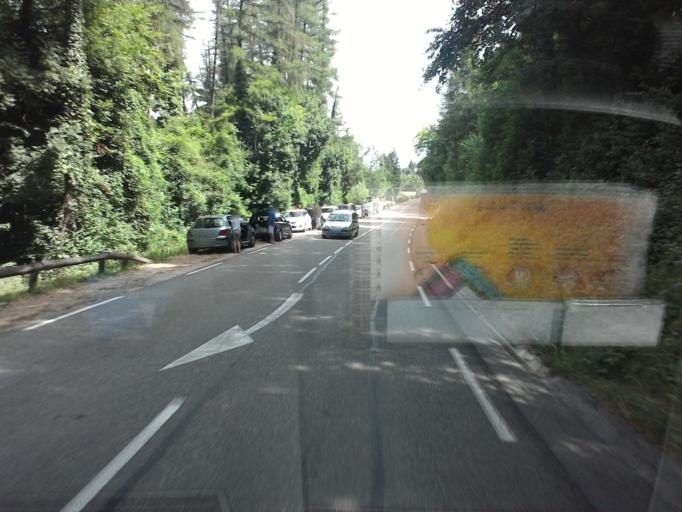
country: FR
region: Rhone-Alpes
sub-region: Departement de l'Isere
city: Charavines
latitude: 45.4405
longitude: 5.5256
